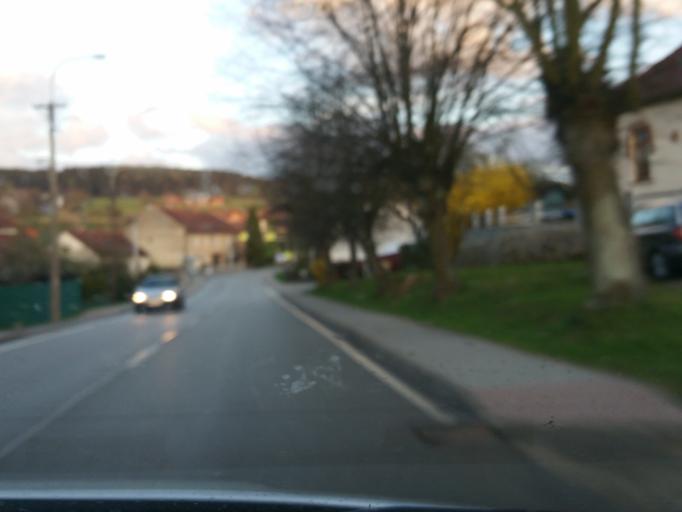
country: CZ
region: South Moravian
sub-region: Okres Blansko
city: Boskovice
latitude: 49.4721
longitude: 16.7175
